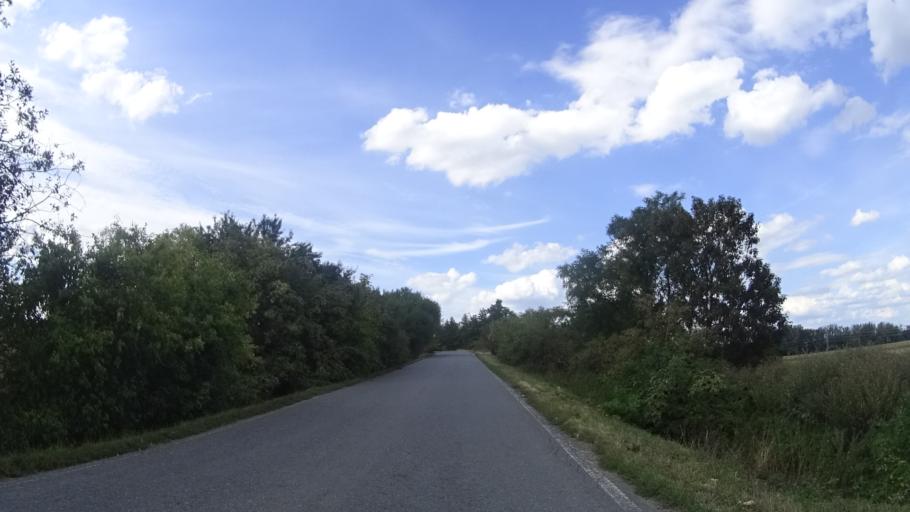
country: CZ
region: Olomoucky
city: Bila Lhota
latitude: 49.7307
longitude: 16.9803
